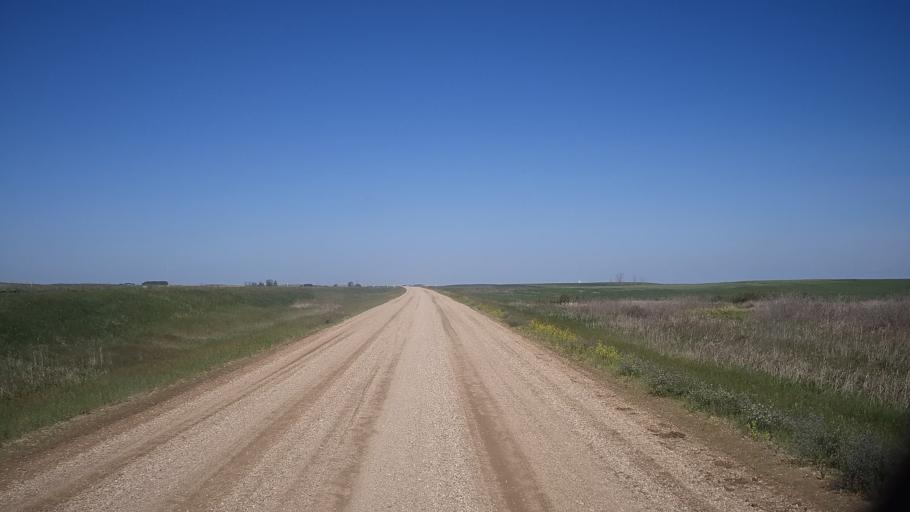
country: CA
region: Saskatchewan
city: Watrous
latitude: 51.8451
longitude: -105.9192
